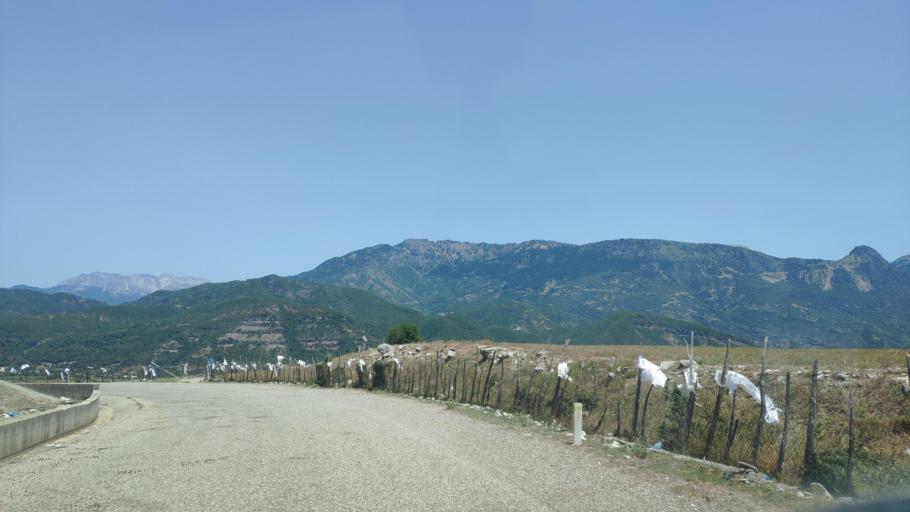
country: GR
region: Thessaly
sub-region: Nomos Kardhitsas
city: Anthiro
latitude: 39.1535
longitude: 21.3855
